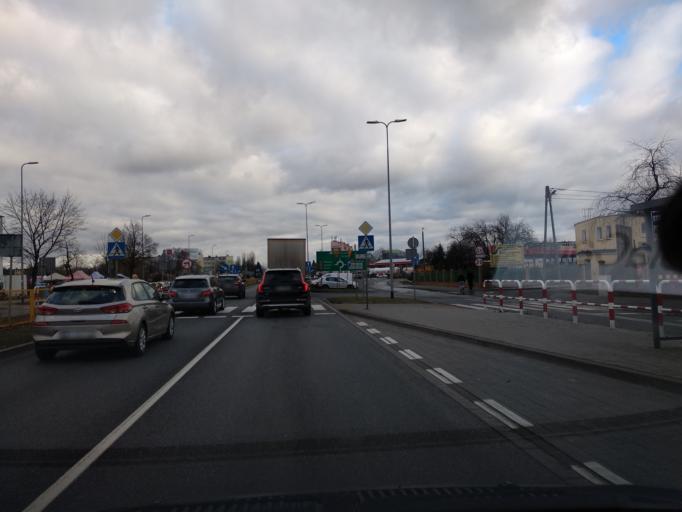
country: PL
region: Greater Poland Voivodeship
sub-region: Kalisz
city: Kalisz
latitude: 51.7470
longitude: 18.0608
